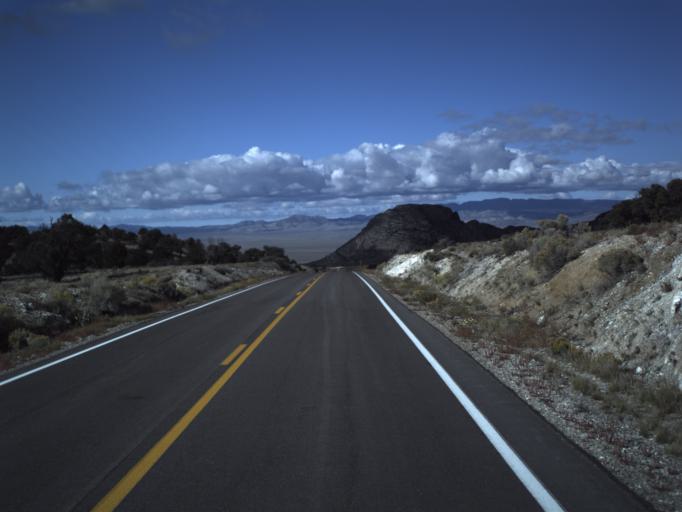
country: US
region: Utah
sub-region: Beaver County
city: Milford
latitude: 38.5166
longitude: -113.5542
